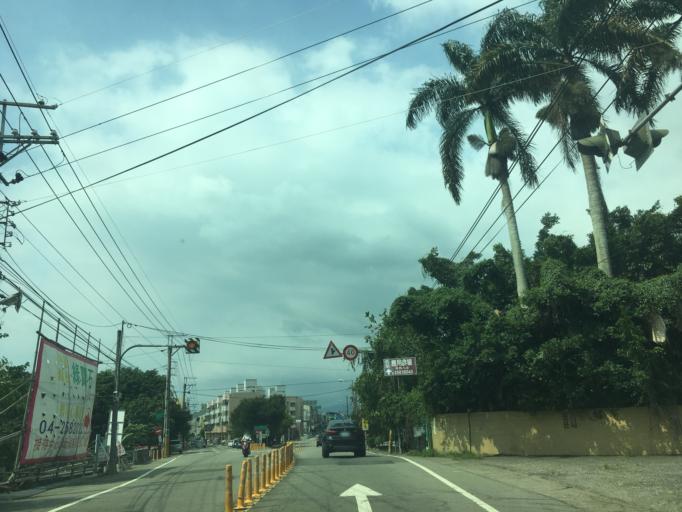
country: TW
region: Taiwan
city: Fengyuan
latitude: 24.2373
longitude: 120.8058
